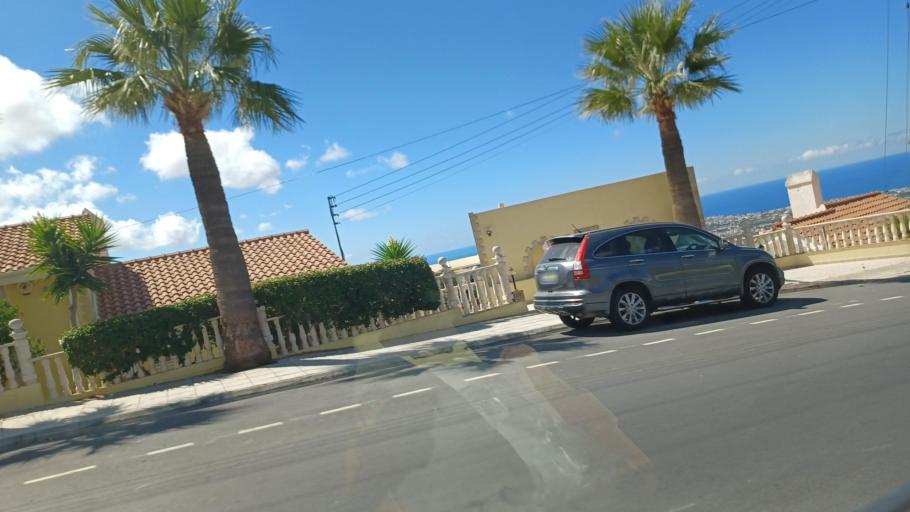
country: CY
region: Pafos
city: Tala
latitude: 34.8397
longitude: 32.4393
